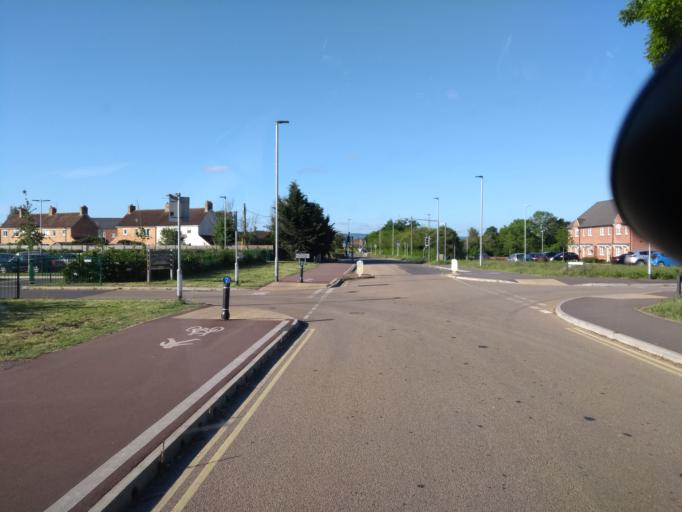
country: GB
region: England
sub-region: Somerset
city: Creech Saint Michael
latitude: 51.0359
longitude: -3.0570
